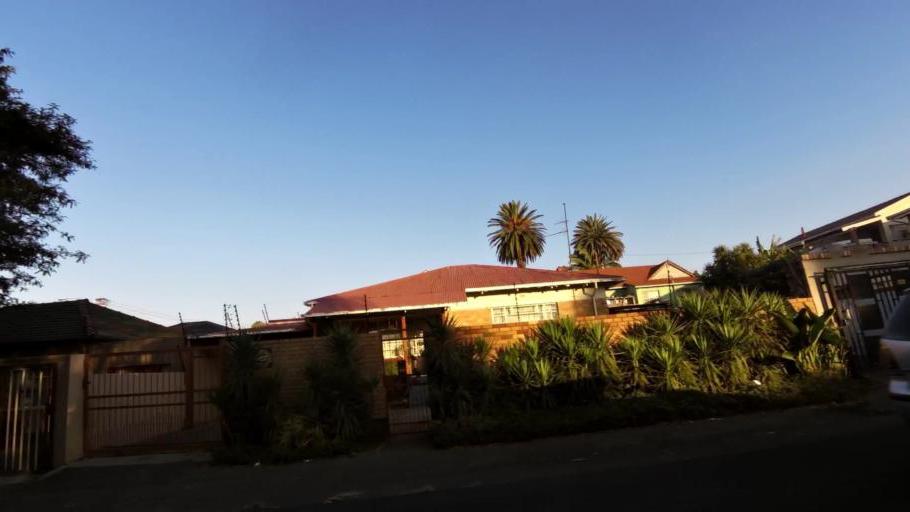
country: ZA
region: Gauteng
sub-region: City of Johannesburg Metropolitan Municipality
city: Roodepoort
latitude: -26.1711
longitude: 27.9598
